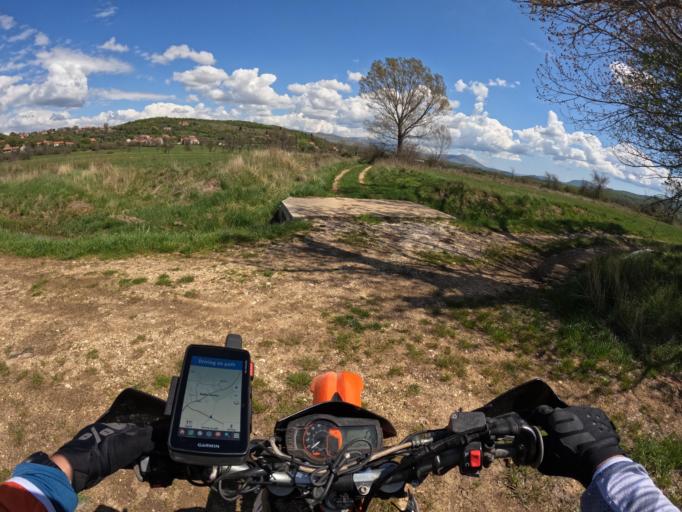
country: HR
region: Sibensko-Kniniska
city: Drnis
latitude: 43.8530
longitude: 16.2271
